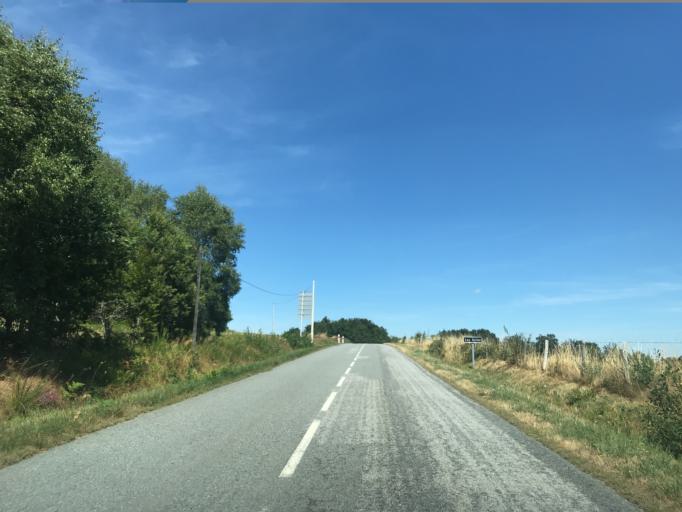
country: FR
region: Limousin
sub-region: Departement de la Creuse
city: La Courtine
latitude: 45.7447
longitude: 2.1413
